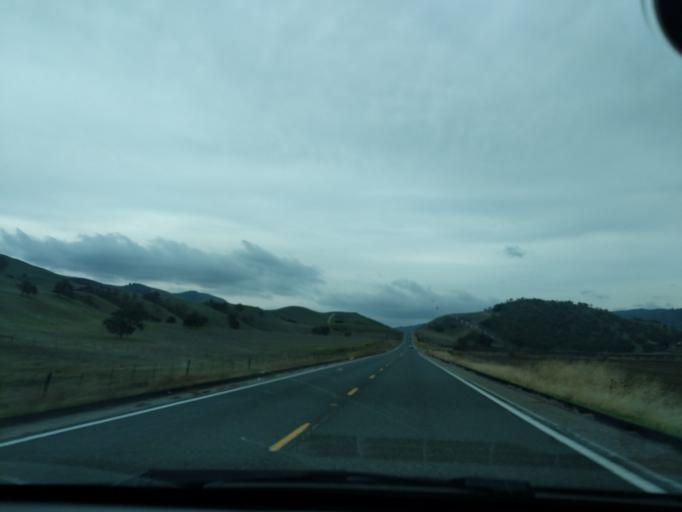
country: US
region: California
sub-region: San Benito County
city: Ridgemark
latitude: 36.6580
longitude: -121.2434
